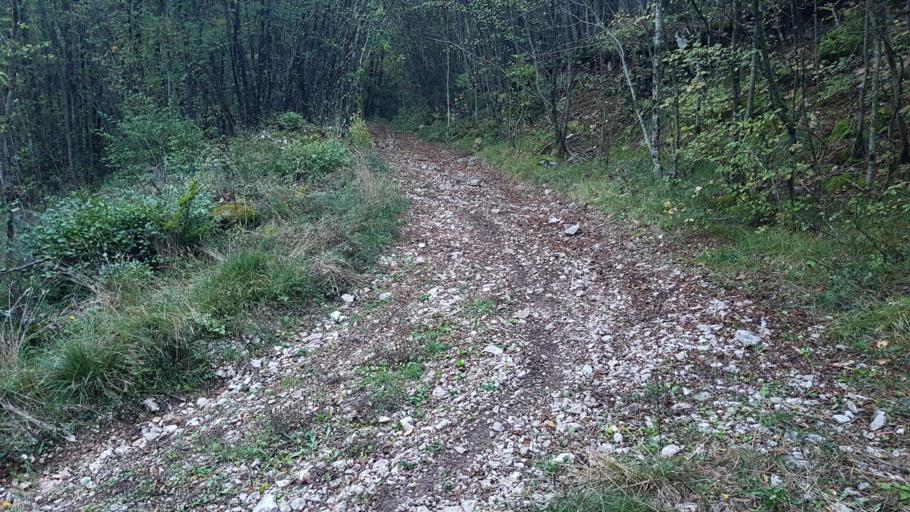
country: HR
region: Istarska
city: Buzet
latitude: 45.3982
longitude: 14.1290
